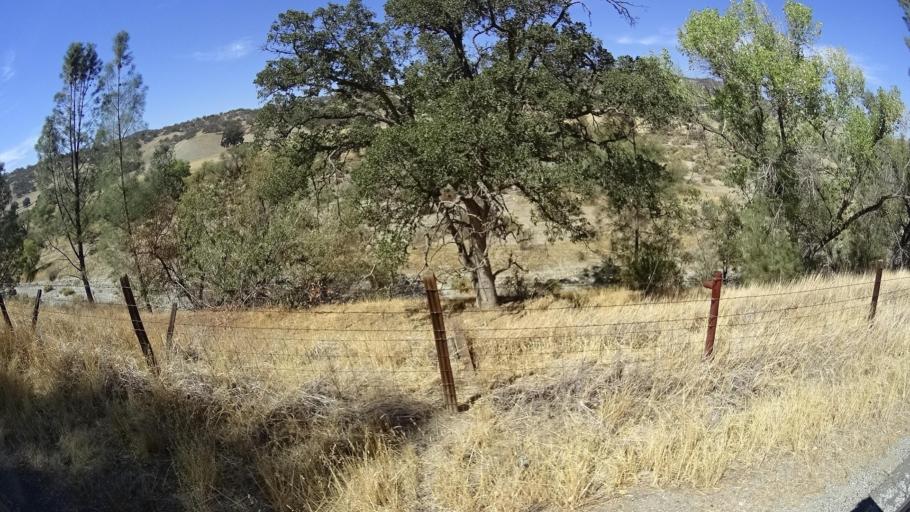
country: US
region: California
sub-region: San Luis Obispo County
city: San Miguel
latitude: 35.9311
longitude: -120.6761
